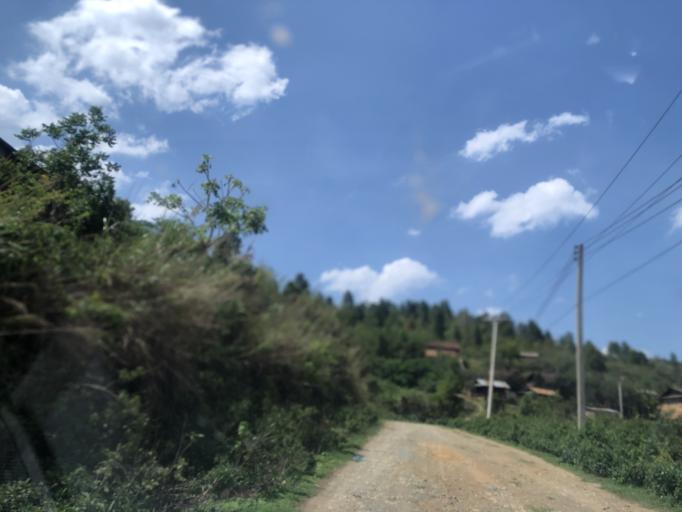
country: LA
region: Phongsali
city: Phongsali
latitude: 21.4057
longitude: 102.2326
